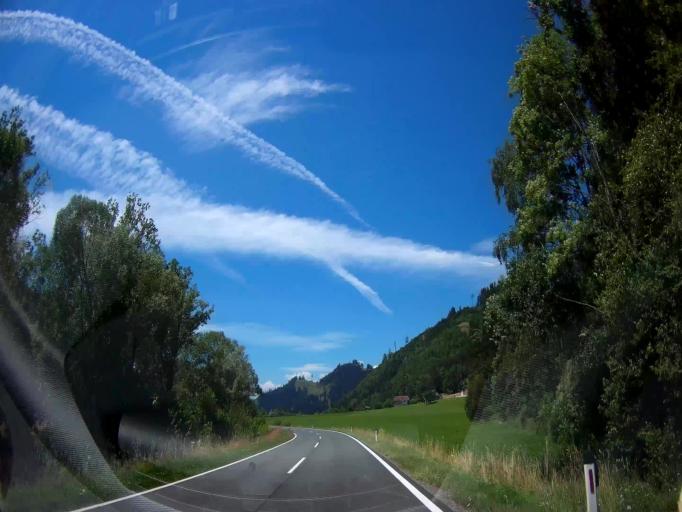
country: AT
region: Carinthia
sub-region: Politischer Bezirk Sankt Veit an der Glan
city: Micheldorf
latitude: 46.9018
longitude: 14.4173
